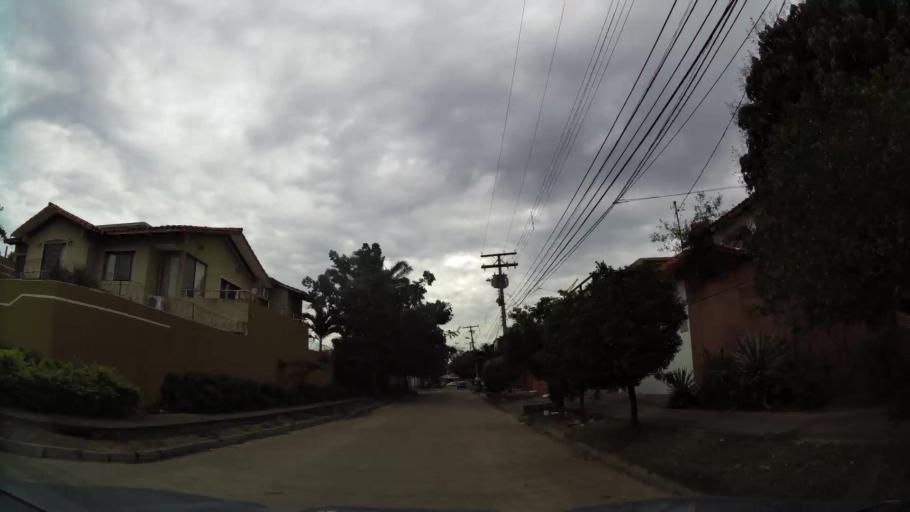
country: BO
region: Santa Cruz
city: Santa Cruz de la Sierra
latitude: -17.7510
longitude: -63.1788
